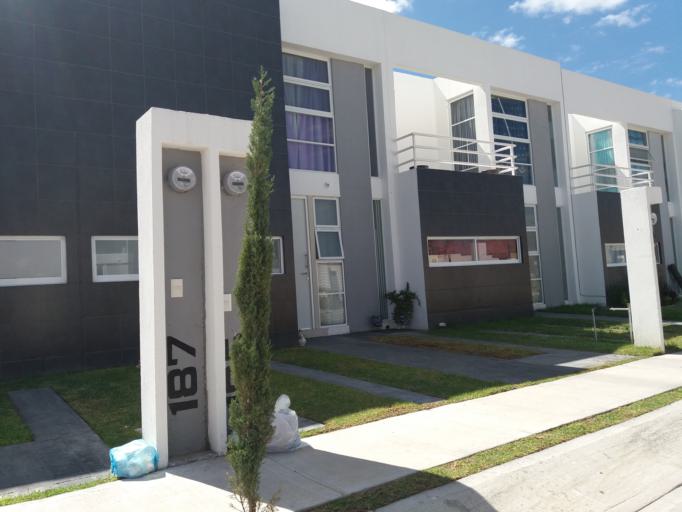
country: MX
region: Aguascalientes
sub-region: Aguascalientes
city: San Sebastian [Fraccionamiento]
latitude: 21.8313
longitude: -102.3009
